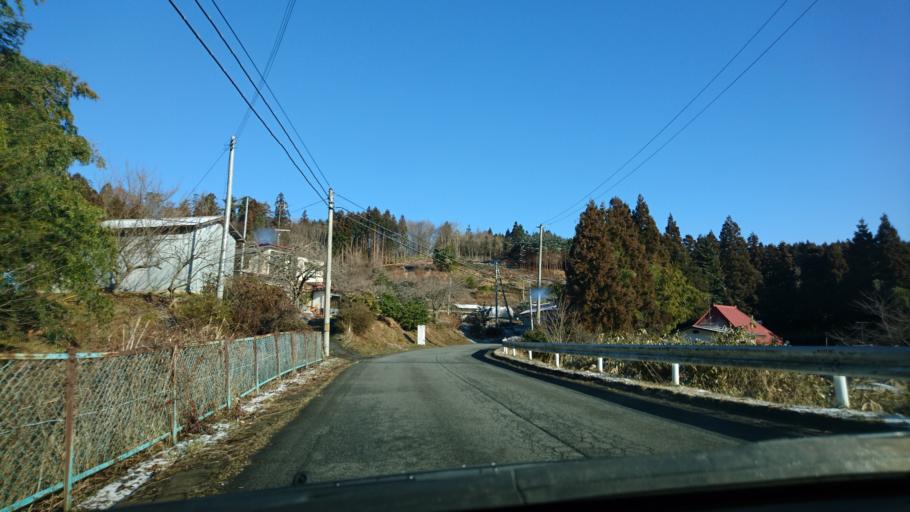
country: JP
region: Iwate
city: Ichinoseki
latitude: 38.8749
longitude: 141.3150
